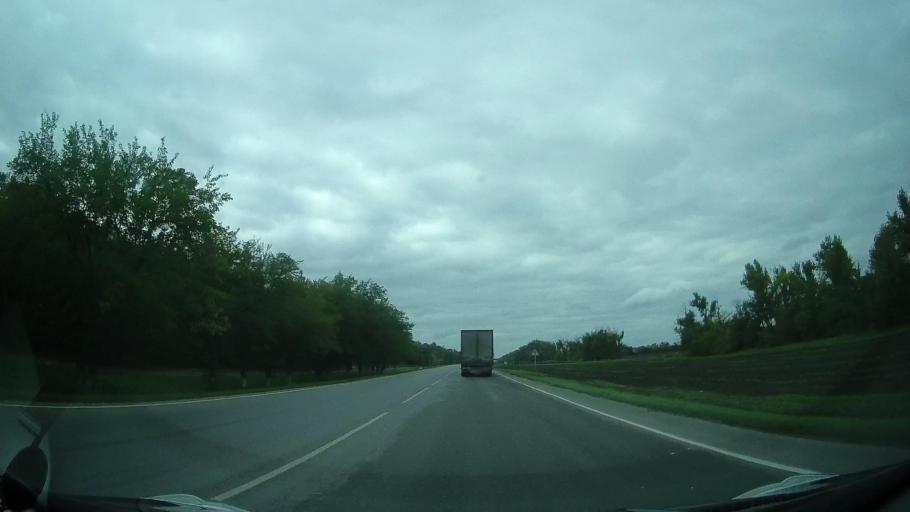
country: RU
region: Rostov
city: Yegorlykskaya
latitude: 46.6227
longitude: 40.5954
